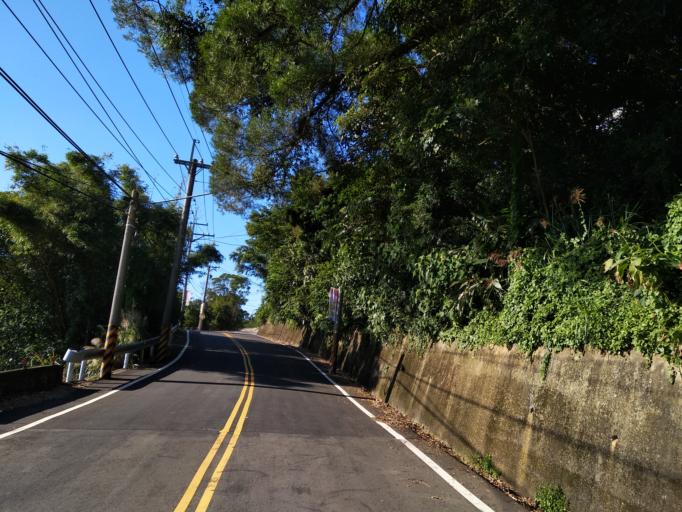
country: TW
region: Taiwan
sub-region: Hsinchu
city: Zhubei
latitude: 24.8681
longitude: 121.0973
